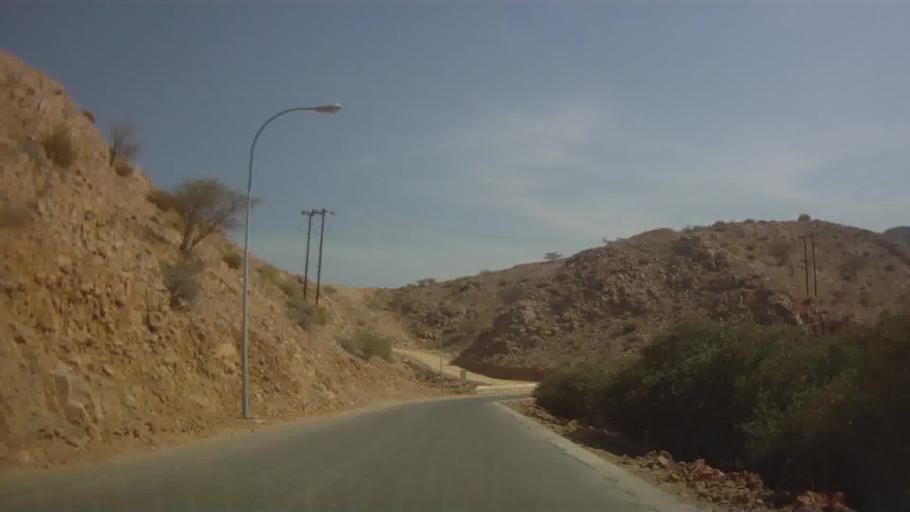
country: OM
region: Muhafazat Masqat
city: Muscat
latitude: 23.5076
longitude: 58.7323
